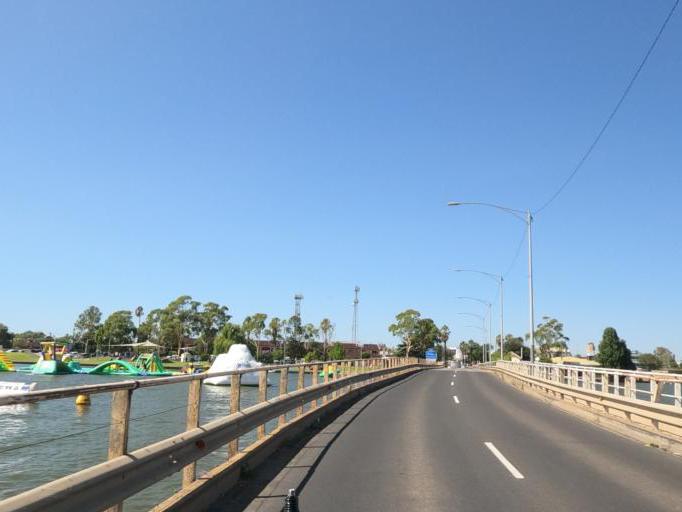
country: AU
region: Victoria
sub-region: Moira
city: Yarrawonga
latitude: -36.0062
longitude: 146.0051
